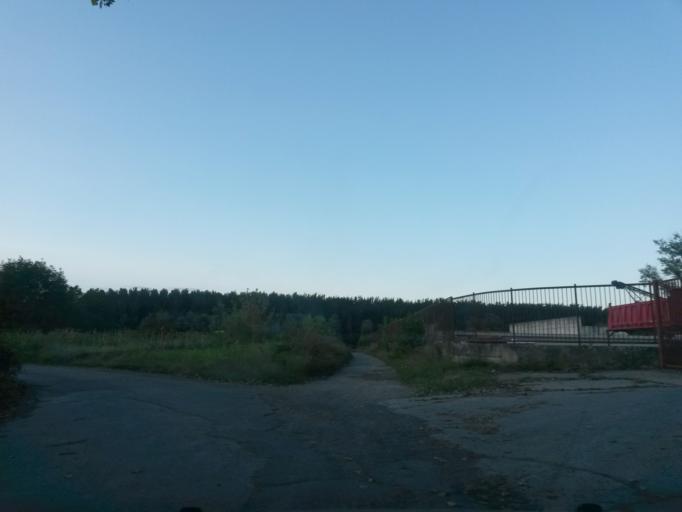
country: HR
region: Osjecko-Baranjska
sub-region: Grad Osijek
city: Osijek
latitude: 45.5607
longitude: 18.7354
